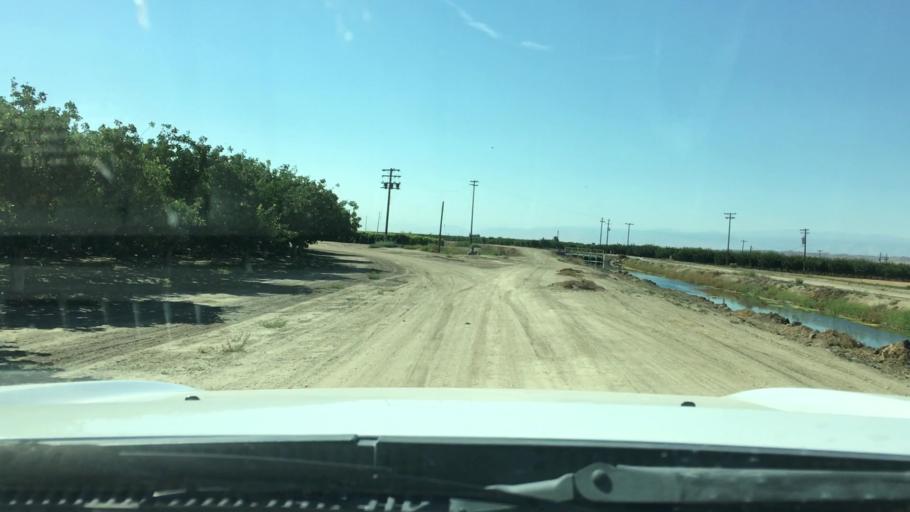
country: US
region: California
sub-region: Kern County
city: Buttonwillow
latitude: 35.3665
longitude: -119.3963
